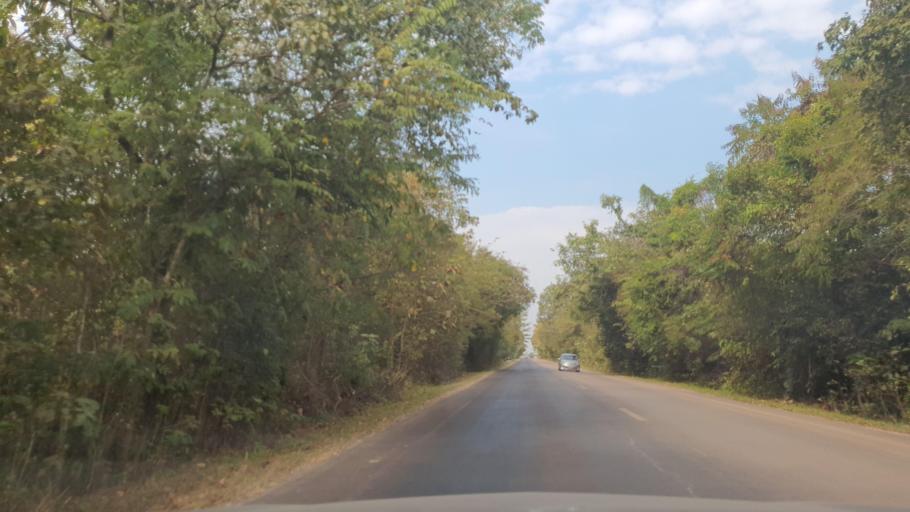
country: TH
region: Changwat Bueng Kan
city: Si Wilai
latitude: 18.2902
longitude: 103.8229
